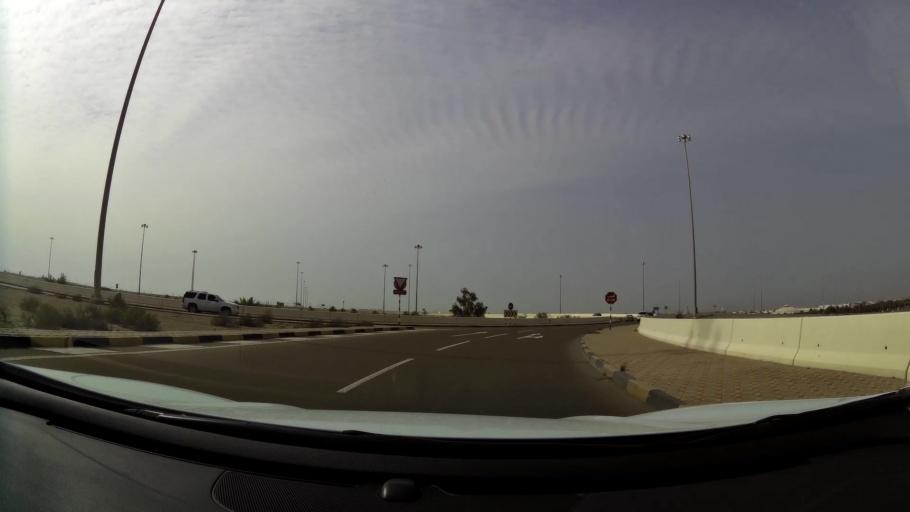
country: AE
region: Abu Dhabi
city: Abu Dhabi
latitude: 24.5641
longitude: 54.6973
